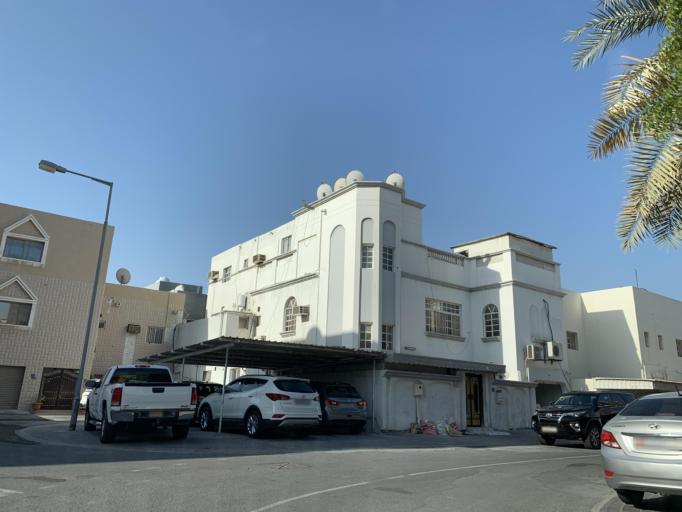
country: BH
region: Muharraq
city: Al Muharraq
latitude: 26.2653
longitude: 50.6049
